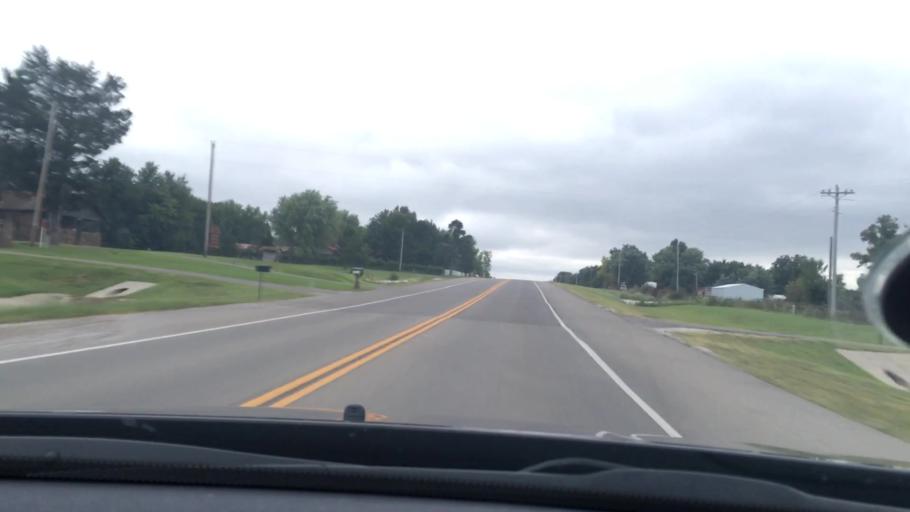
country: US
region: Oklahoma
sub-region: Sequoyah County
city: Vian
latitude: 35.6066
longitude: -94.9763
